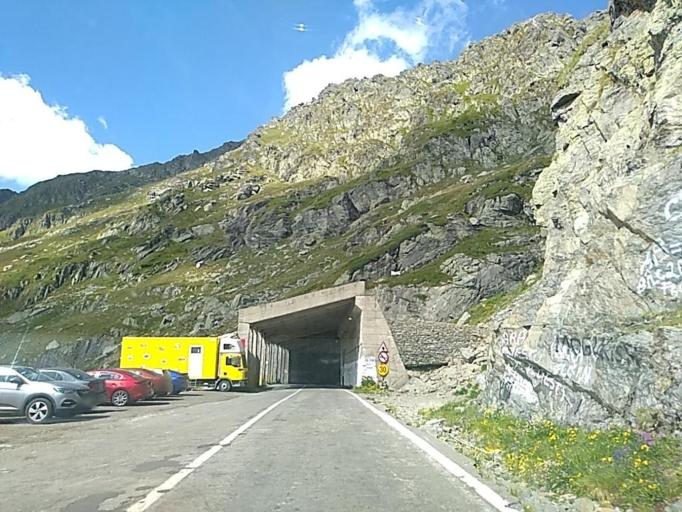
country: RO
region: Sibiu
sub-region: Comuna Cartisoara
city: Cartisoara
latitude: 45.5949
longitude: 24.6201
